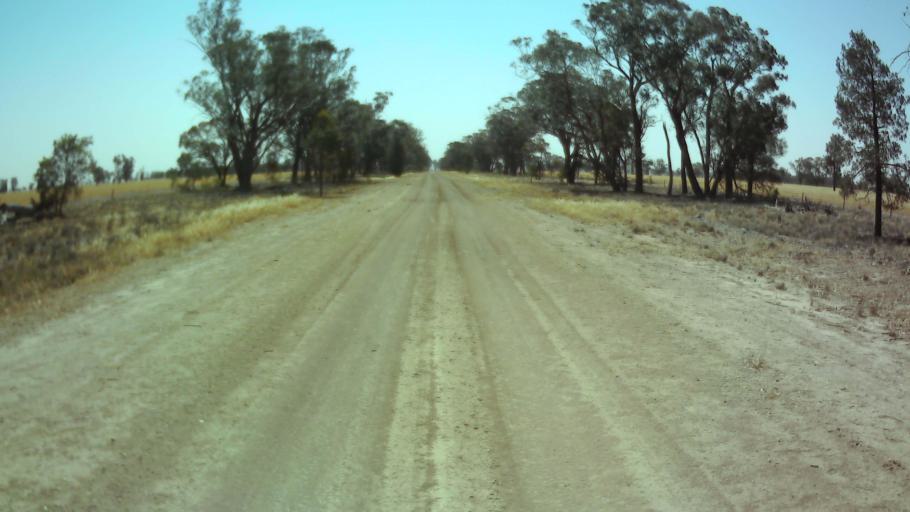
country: AU
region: New South Wales
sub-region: Weddin
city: Grenfell
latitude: -33.9452
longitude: 147.8156
